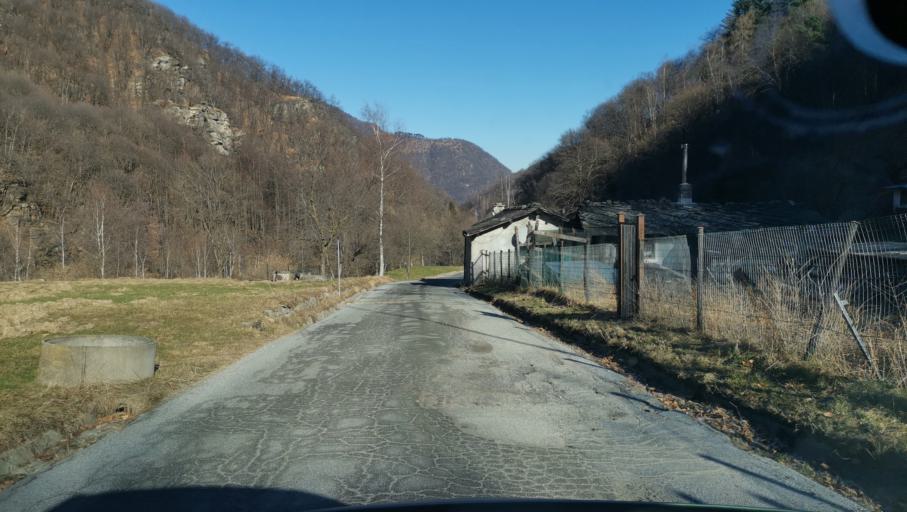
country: IT
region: Piedmont
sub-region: Provincia di Torino
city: Rora
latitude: 44.7734
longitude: 7.2052
